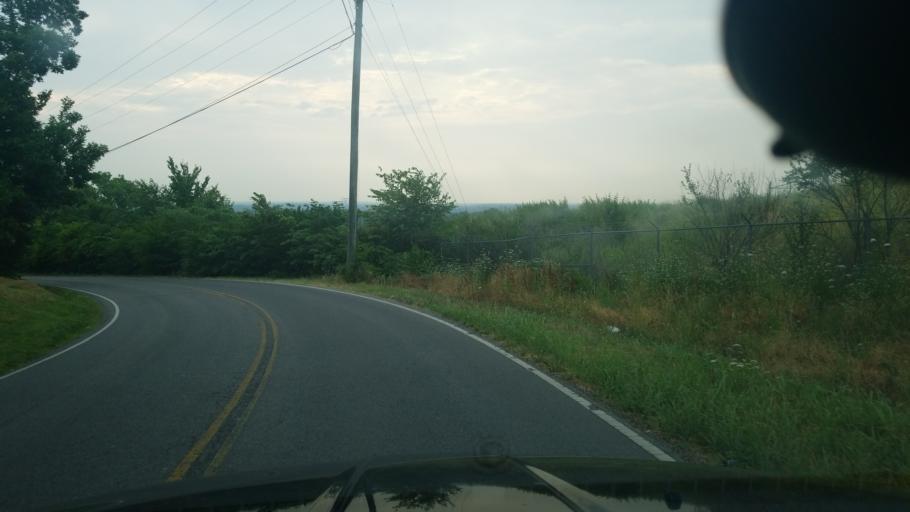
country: US
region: Tennessee
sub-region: Davidson County
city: Goodlettsville
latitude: 36.2490
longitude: -86.7450
